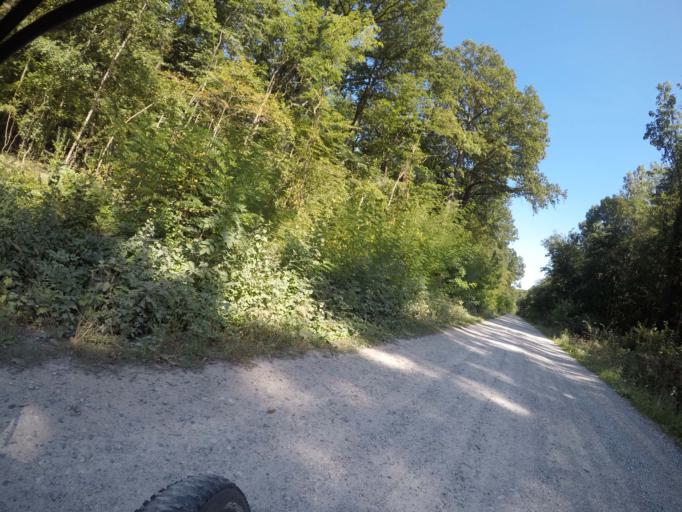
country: AT
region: Lower Austria
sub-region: Politischer Bezirk Bruck an der Leitha
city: Mannersdorf am Leithagebirge
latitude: 47.9555
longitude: 16.5977
